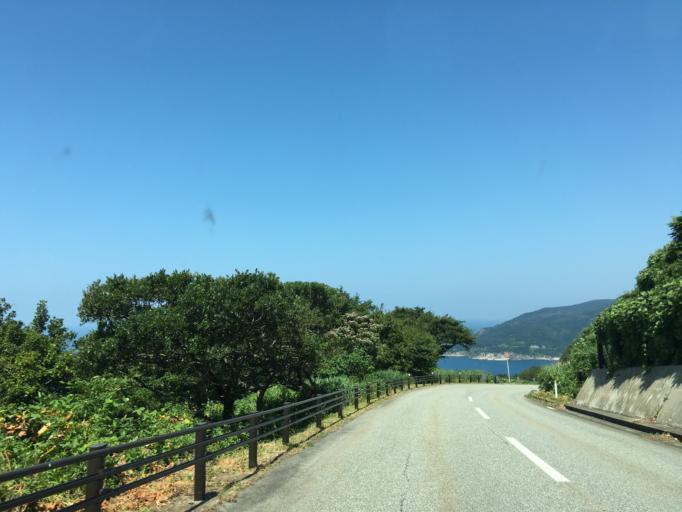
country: JP
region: Akita
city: Tenno
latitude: 39.8883
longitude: 139.7407
